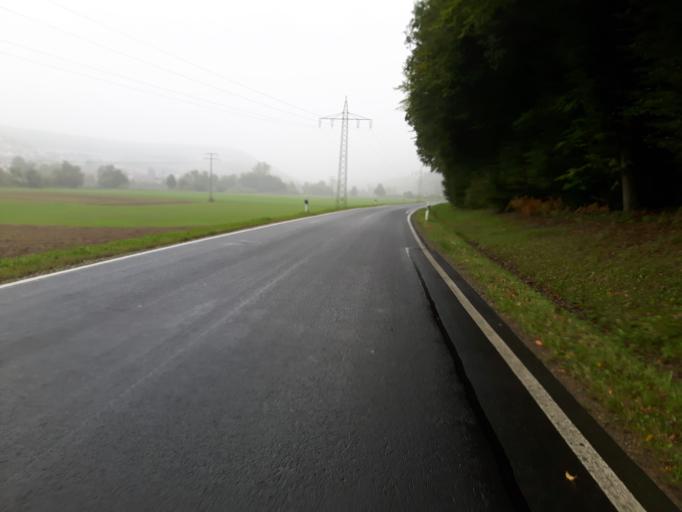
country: DE
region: Bavaria
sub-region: Regierungsbezirk Unterfranken
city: Gemunden
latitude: 50.0506
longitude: 9.6912
